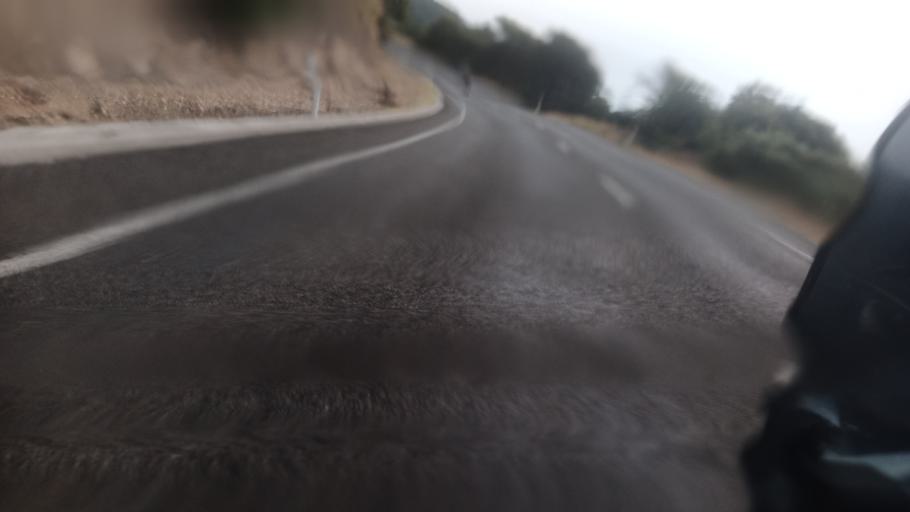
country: NZ
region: Bay of Plenty
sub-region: Opotiki District
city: Opotiki
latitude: -37.9104
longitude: 177.5457
